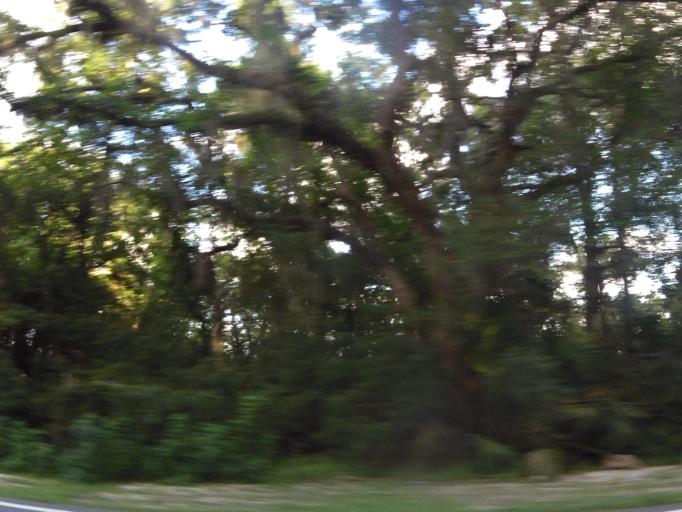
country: US
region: Georgia
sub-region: Glynn County
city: Saint Simon Mills
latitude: 31.1806
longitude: -81.3998
